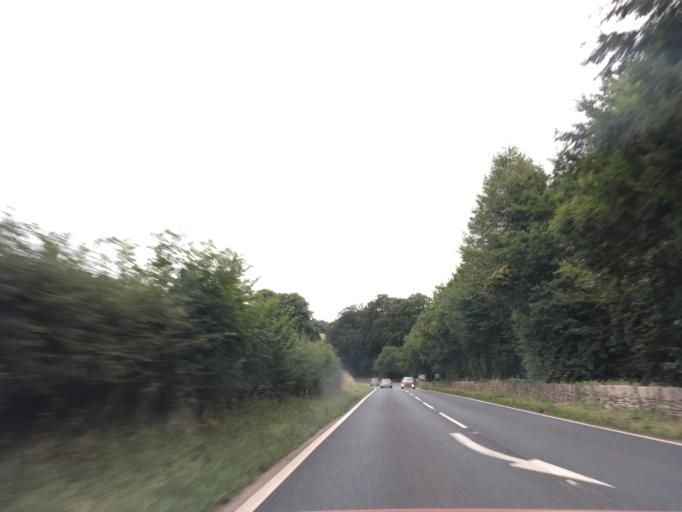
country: GB
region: Wales
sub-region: Sir Powys
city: Brecon
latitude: 51.9462
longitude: -3.4907
